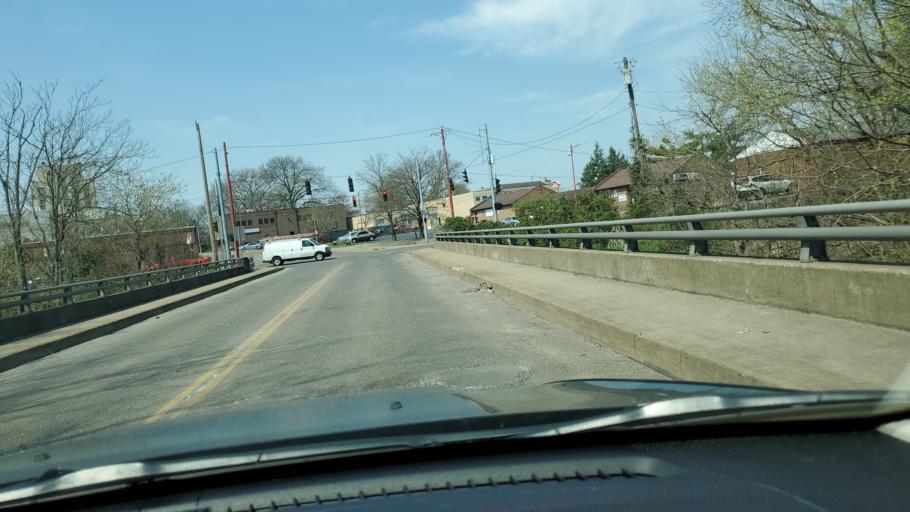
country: US
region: Ohio
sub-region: Trumbull County
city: Niles
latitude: 41.1801
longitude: -80.7629
